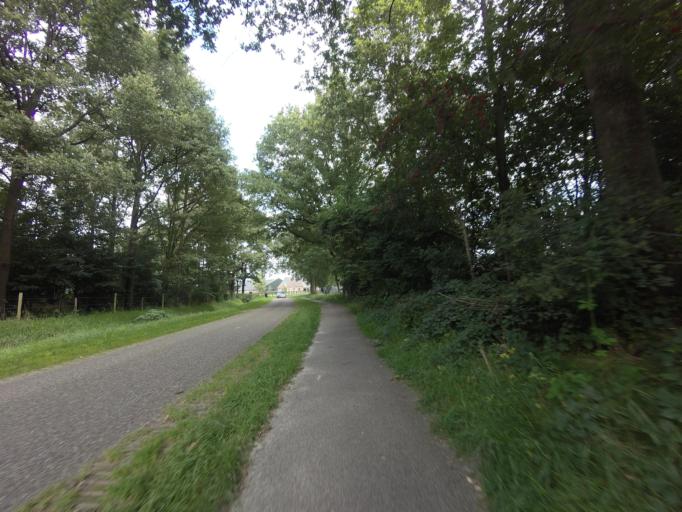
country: NL
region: Drenthe
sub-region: Gemeente Westerveld
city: Havelte
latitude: 52.8565
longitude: 6.2565
